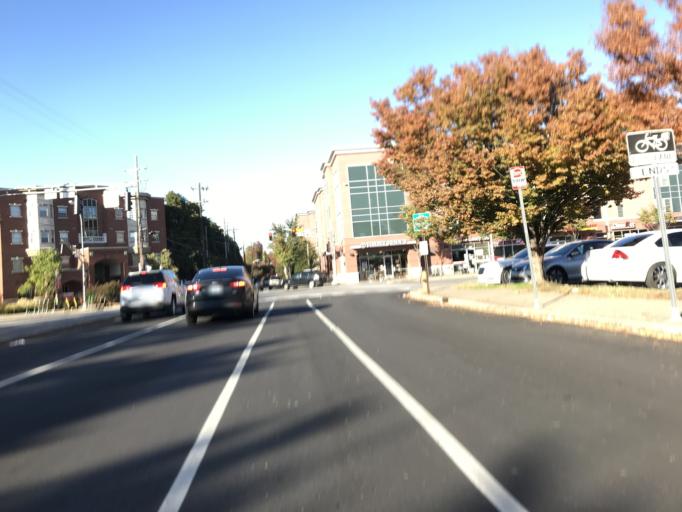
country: US
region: Kentucky
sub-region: Jefferson County
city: Louisville
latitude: 38.2203
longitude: -85.7628
